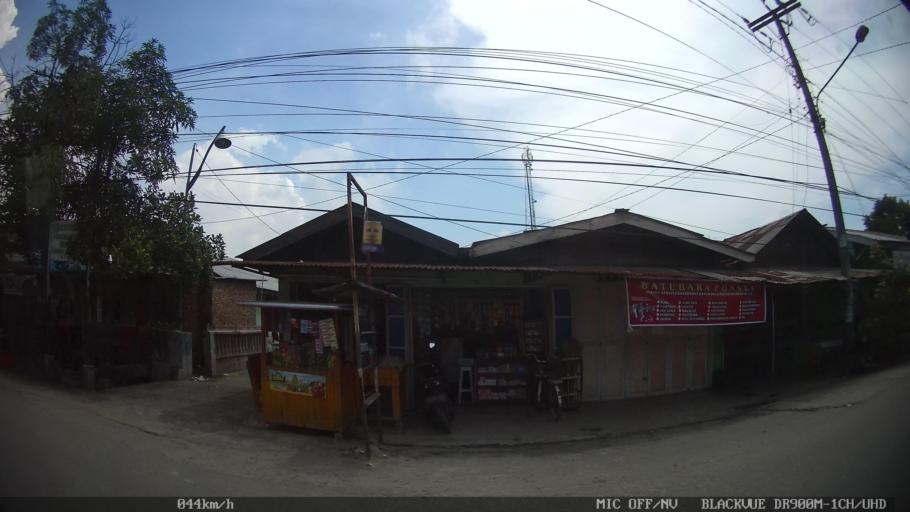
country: ID
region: North Sumatra
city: Labuhan Deli
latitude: 3.6698
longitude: 98.6787
